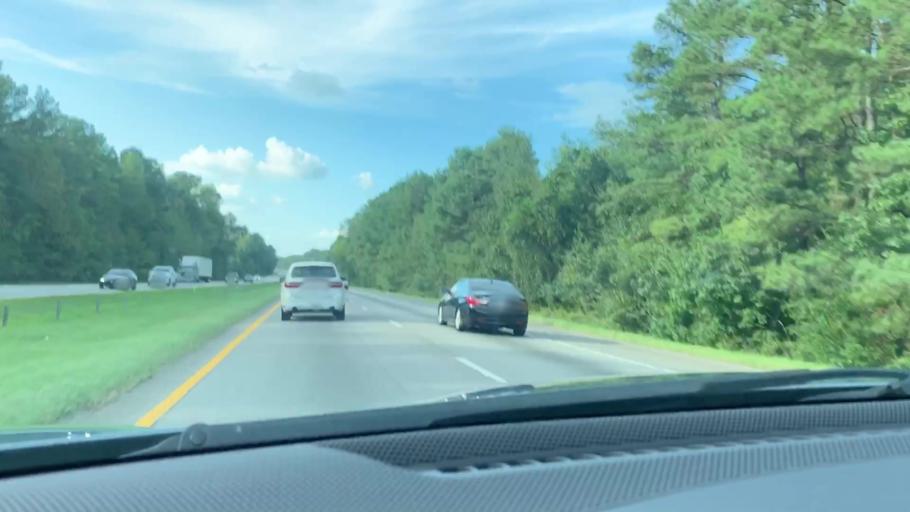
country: US
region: South Carolina
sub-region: Orangeburg County
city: Brookdale
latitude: 33.4908
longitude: -80.7629
